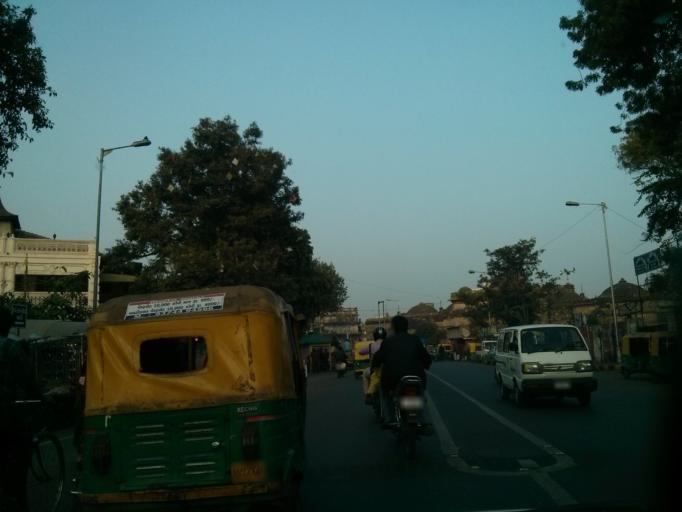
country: IN
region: Gujarat
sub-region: Ahmadabad
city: Ahmedabad
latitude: 23.0351
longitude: 72.5864
